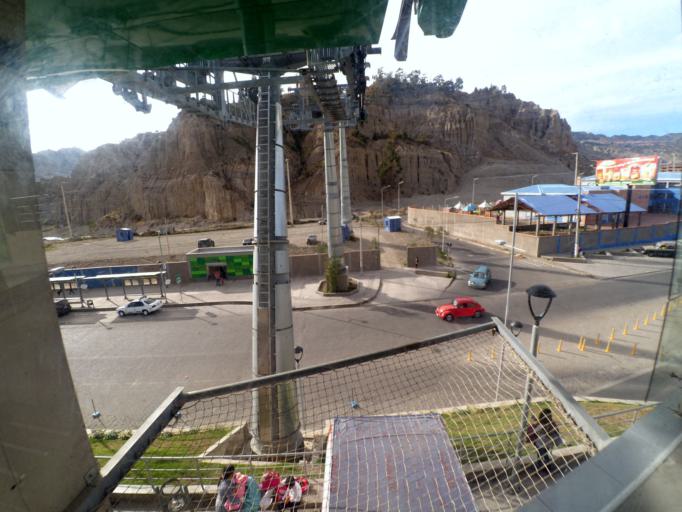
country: BO
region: La Paz
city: La Paz
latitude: -16.5376
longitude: -68.0879
